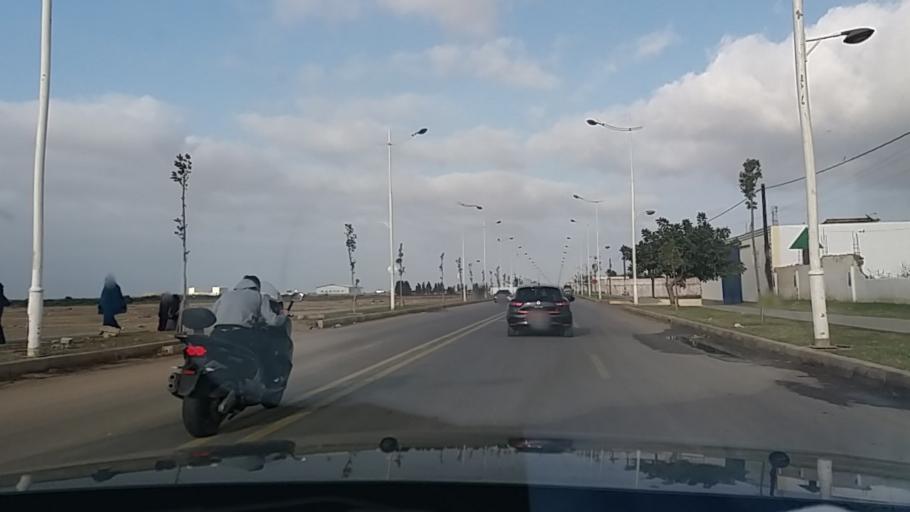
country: MA
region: Tanger-Tetouan
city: Tetouan
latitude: 35.5685
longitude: -5.3343
